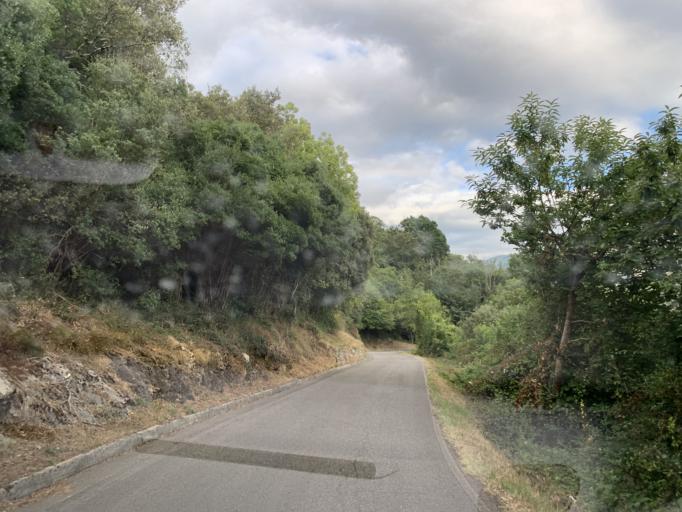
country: ES
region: Asturias
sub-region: Province of Asturias
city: Carrena
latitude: 43.3223
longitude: -4.8559
